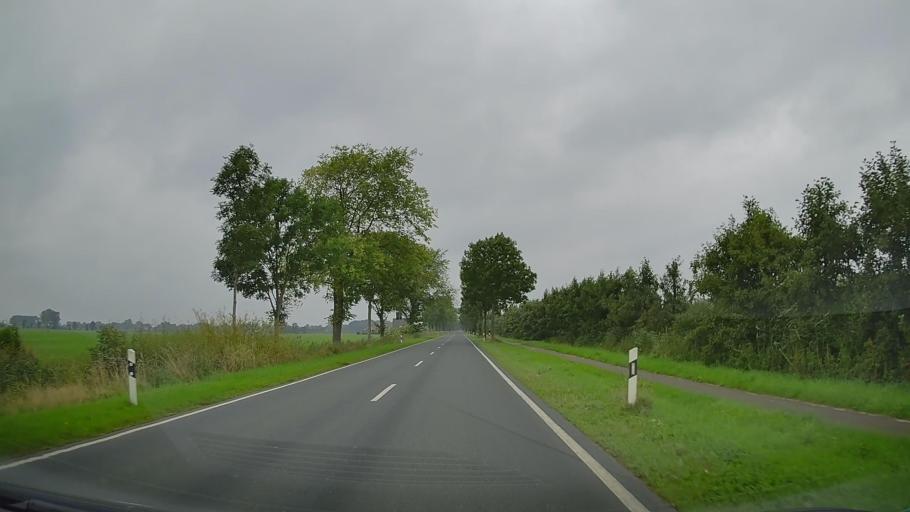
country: DE
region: Lower Saxony
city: Balje
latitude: 53.8142
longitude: 9.1306
